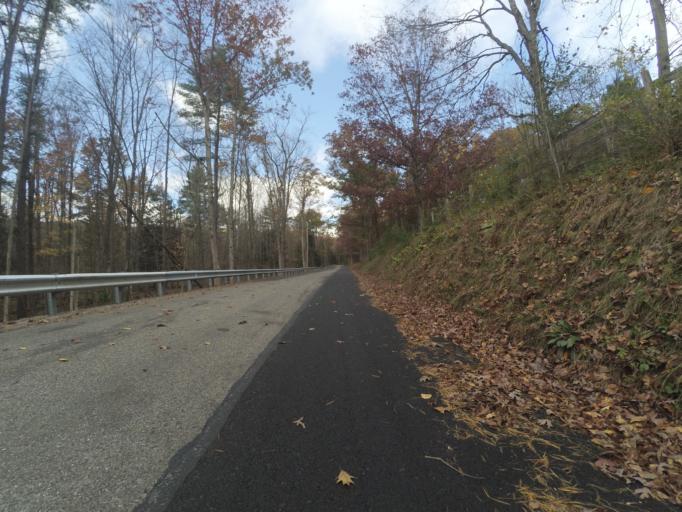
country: US
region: Pennsylvania
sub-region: Centre County
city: Stormstown
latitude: 40.8559
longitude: -77.9810
